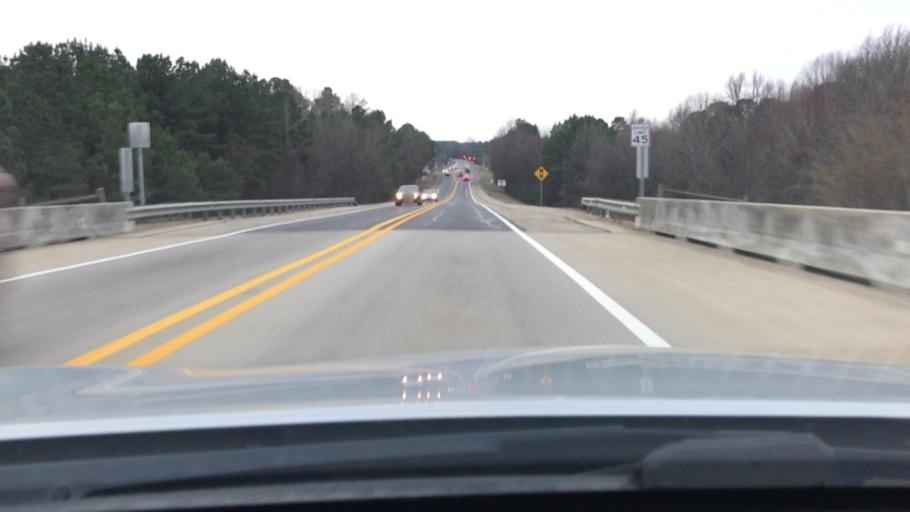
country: US
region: Arkansas
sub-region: Hempstead County
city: Hope
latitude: 33.6716
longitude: -93.5758
